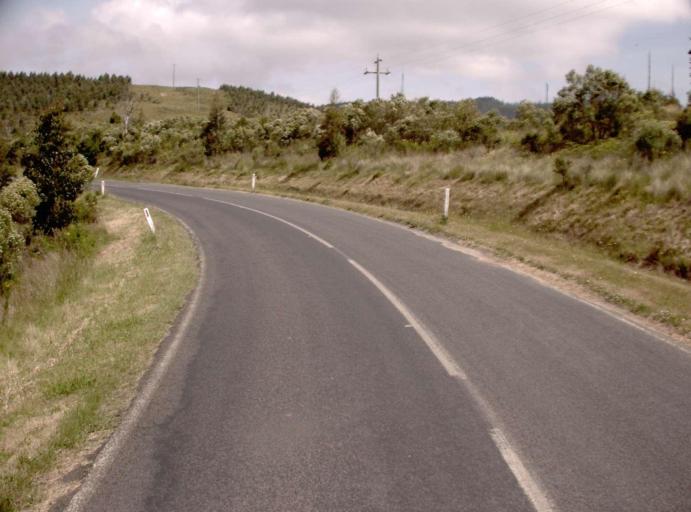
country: AU
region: Victoria
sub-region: Latrobe
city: Traralgon
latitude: -38.3732
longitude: 146.5685
